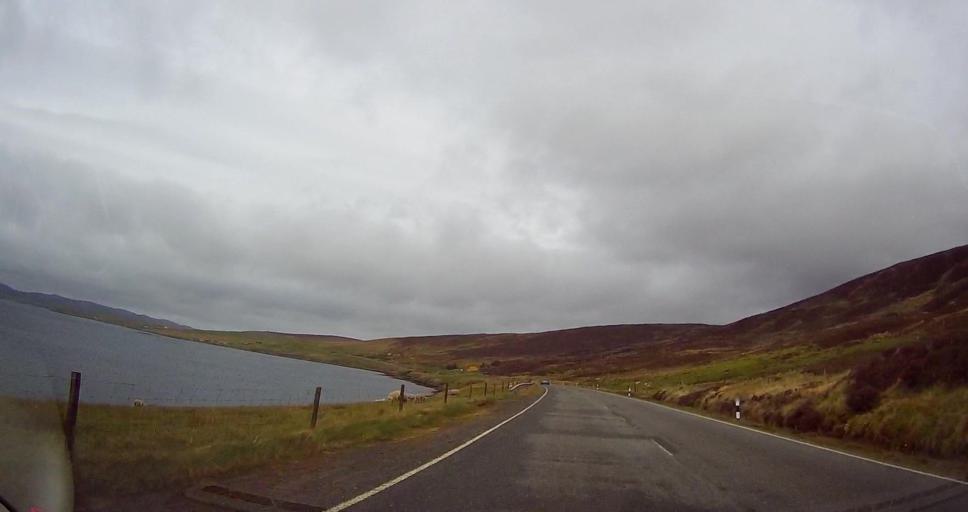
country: GB
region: Scotland
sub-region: Shetland Islands
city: Lerwick
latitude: 60.3656
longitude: -1.2895
